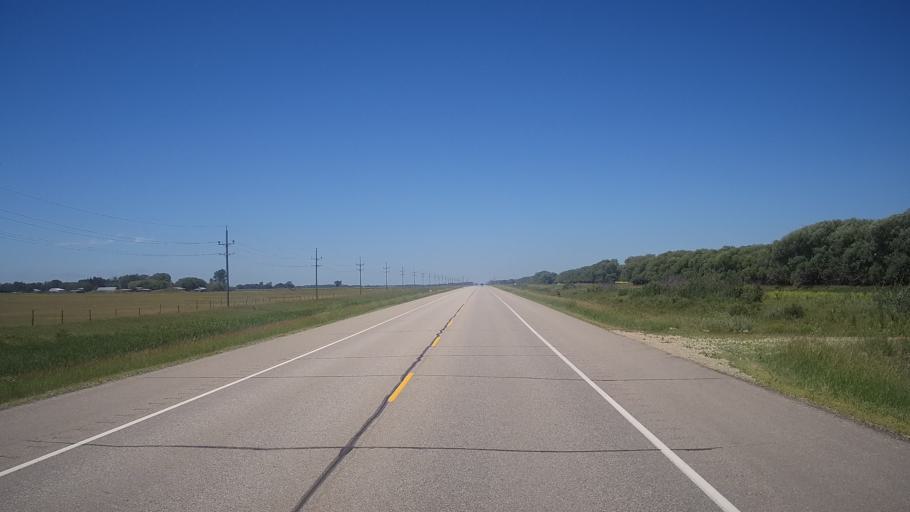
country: CA
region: Manitoba
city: Neepawa
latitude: 50.2257
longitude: -99.0541
